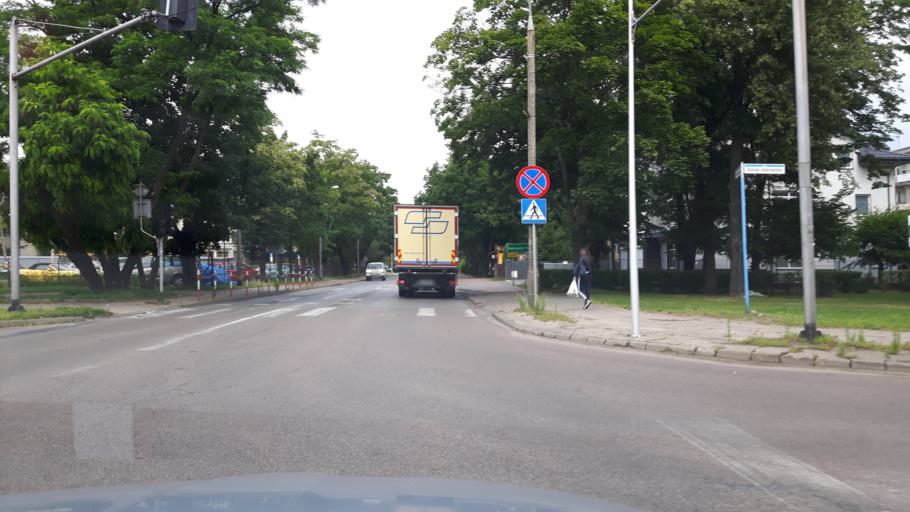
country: PL
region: Masovian Voivodeship
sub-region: Powiat wolominski
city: Nowe Lipiny
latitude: 52.3523
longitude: 21.2606
